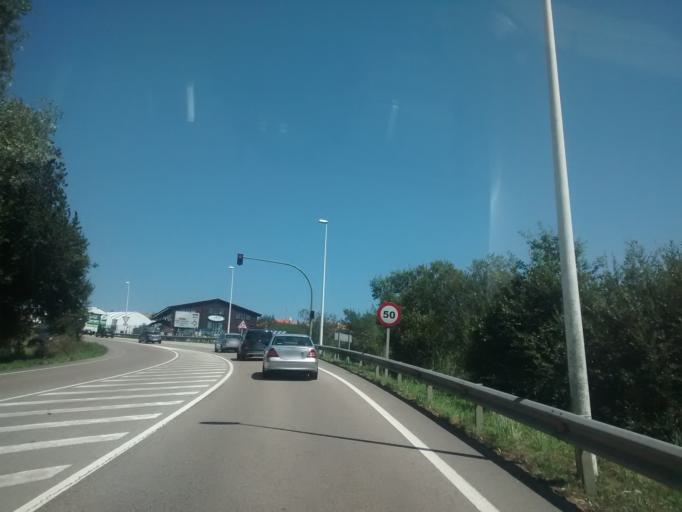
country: ES
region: Cantabria
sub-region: Provincia de Cantabria
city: San Miguel de Meruelo
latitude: 43.4430
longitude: -3.5662
